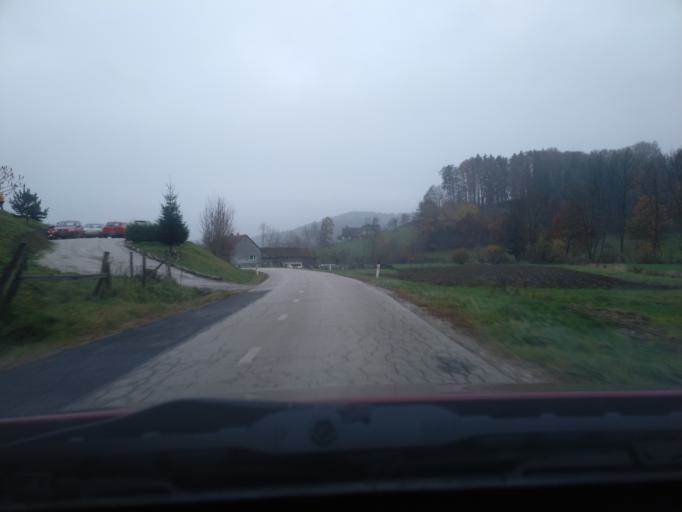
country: SI
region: Kungota
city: Zgornja Kungota
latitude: 46.6585
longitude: 15.6118
